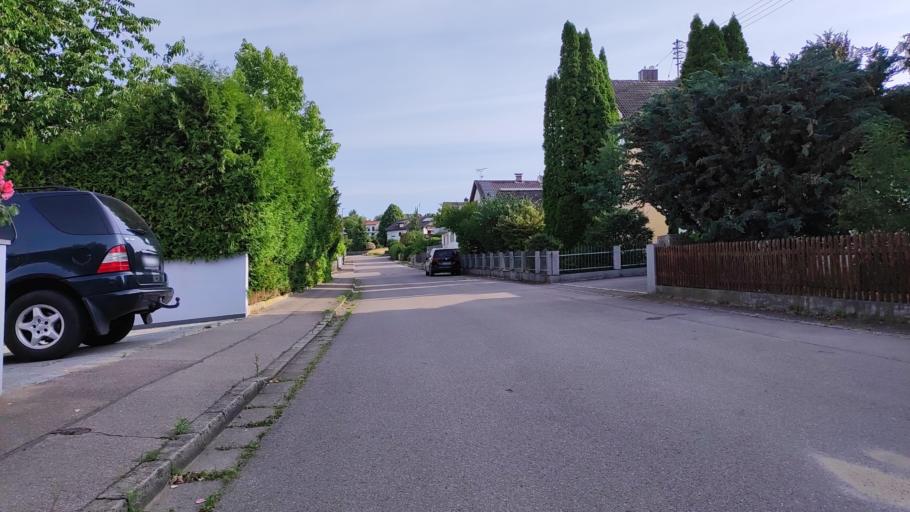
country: DE
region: Bavaria
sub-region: Swabia
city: Horgau
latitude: 48.3975
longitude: 10.6957
